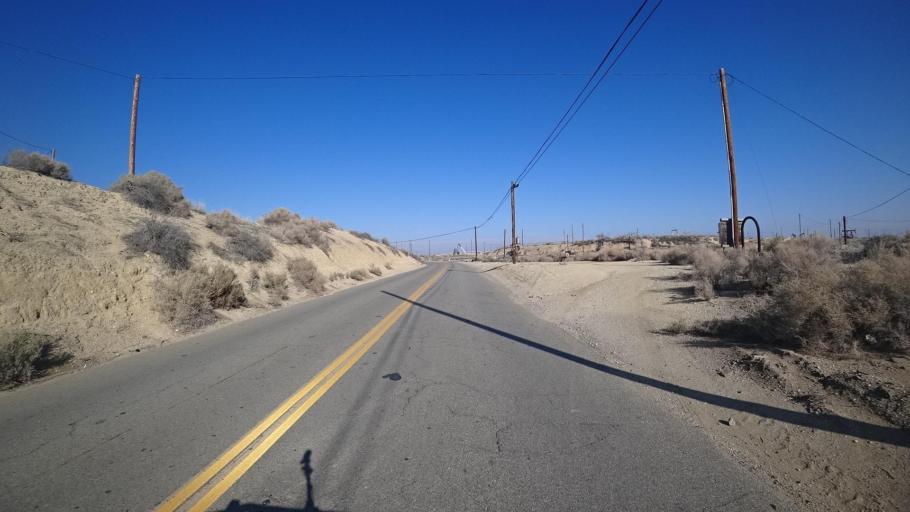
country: US
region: California
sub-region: Kern County
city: Taft Heights
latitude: 35.2207
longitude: -119.6094
